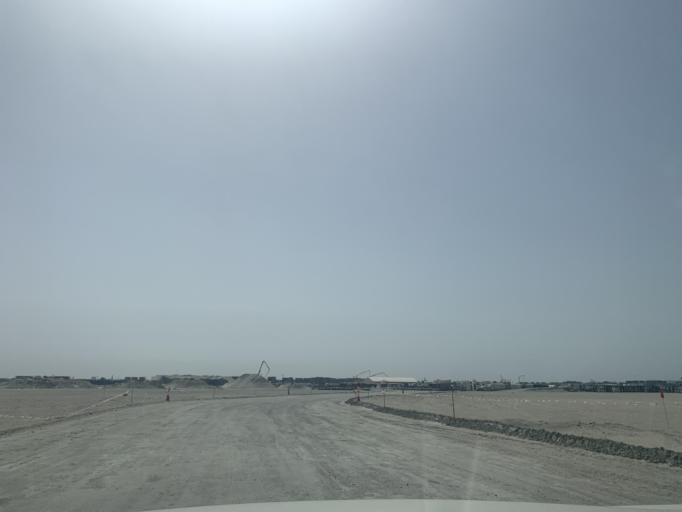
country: BH
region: Northern
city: Sitrah
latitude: 26.1619
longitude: 50.6397
